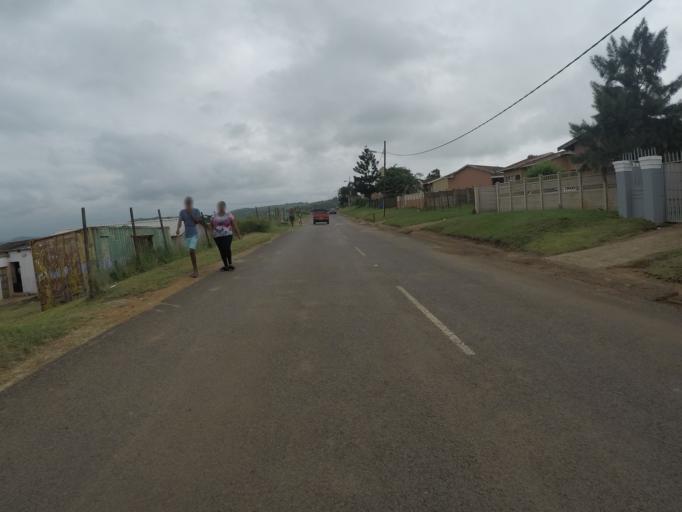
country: ZA
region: KwaZulu-Natal
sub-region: uThungulu District Municipality
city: Empangeni
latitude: -28.7784
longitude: 31.8491
